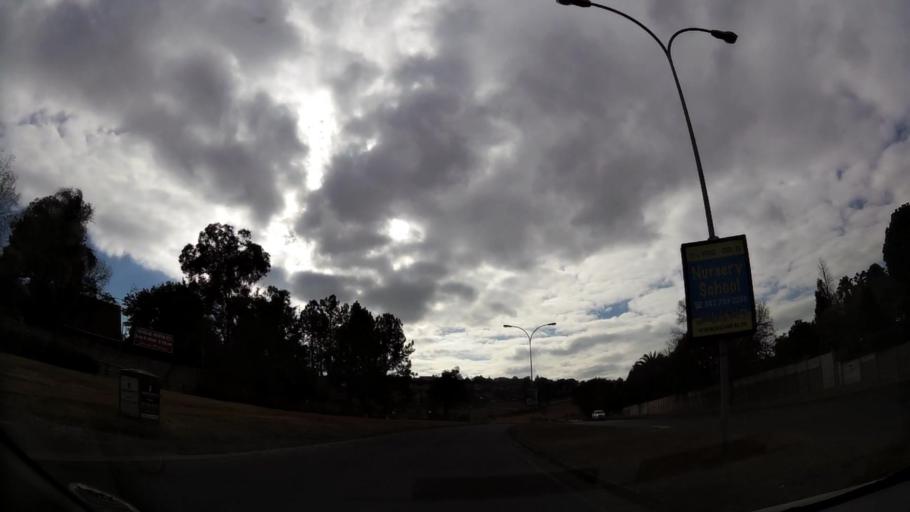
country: ZA
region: Gauteng
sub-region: City of Johannesburg Metropolitan Municipality
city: Roodepoort
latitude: -26.1084
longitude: 27.8565
